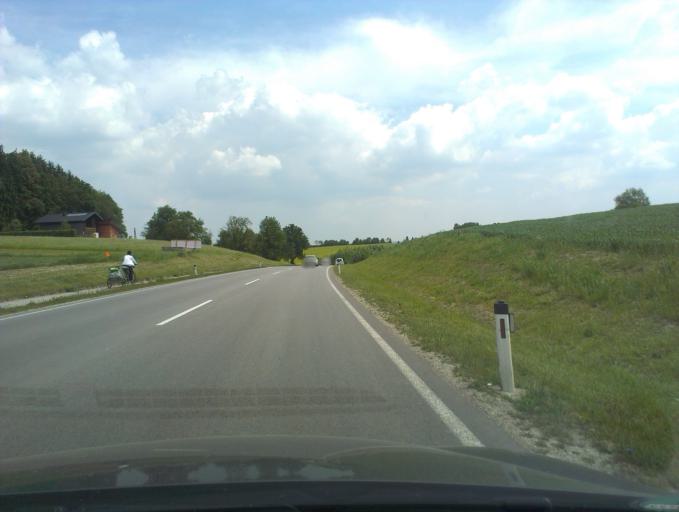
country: AT
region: Upper Austria
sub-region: Politischer Bezirk Ried im Innkreis
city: Ried im Innkreis
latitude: 48.2074
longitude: 13.4455
